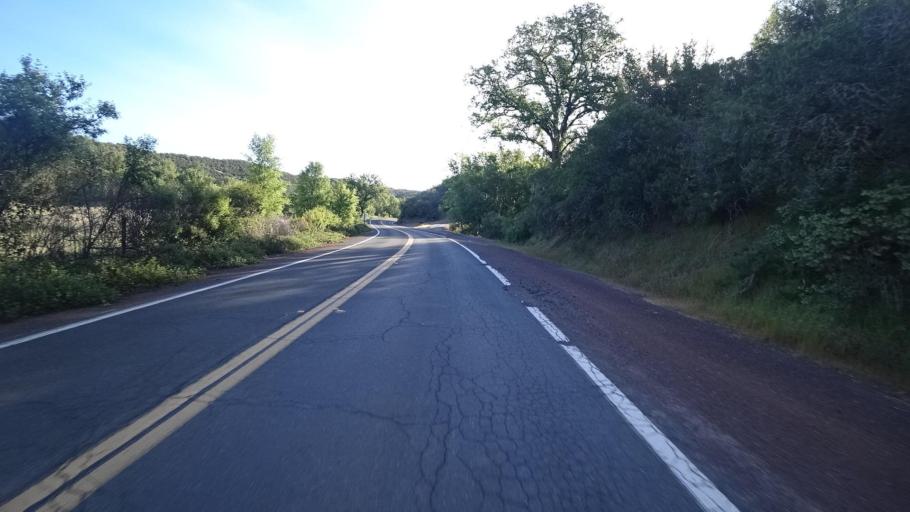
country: US
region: California
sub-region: Lake County
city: North Lakeport
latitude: 39.0915
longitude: -122.9556
